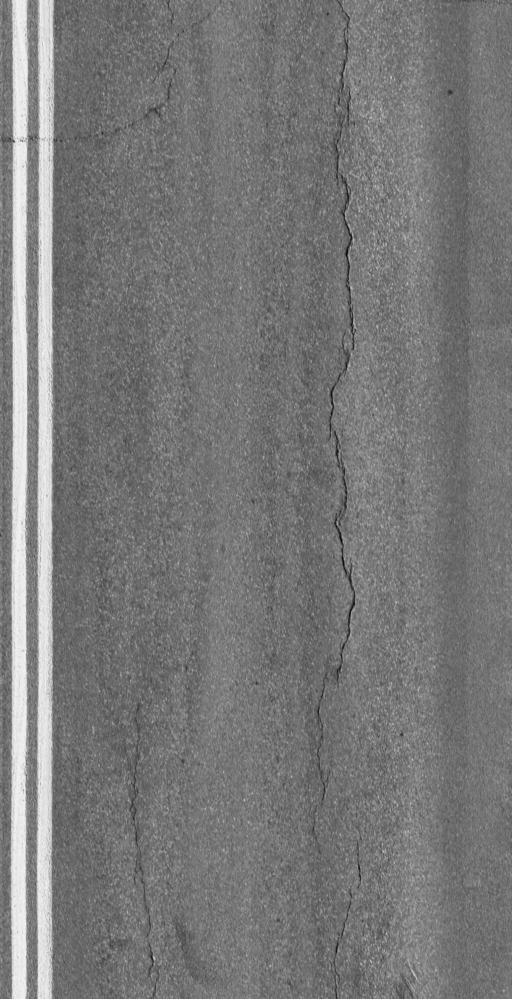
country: US
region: Vermont
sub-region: Chittenden County
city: Hinesburg
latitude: 44.3798
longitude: -73.1779
